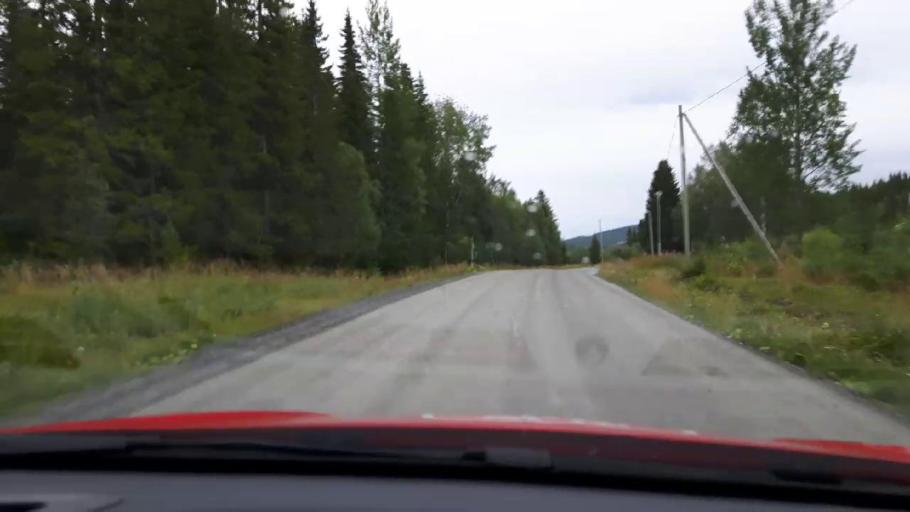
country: SE
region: Jaemtland
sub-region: Are Kommun
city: Jarpen
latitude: 63.4191
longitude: 13.3514
